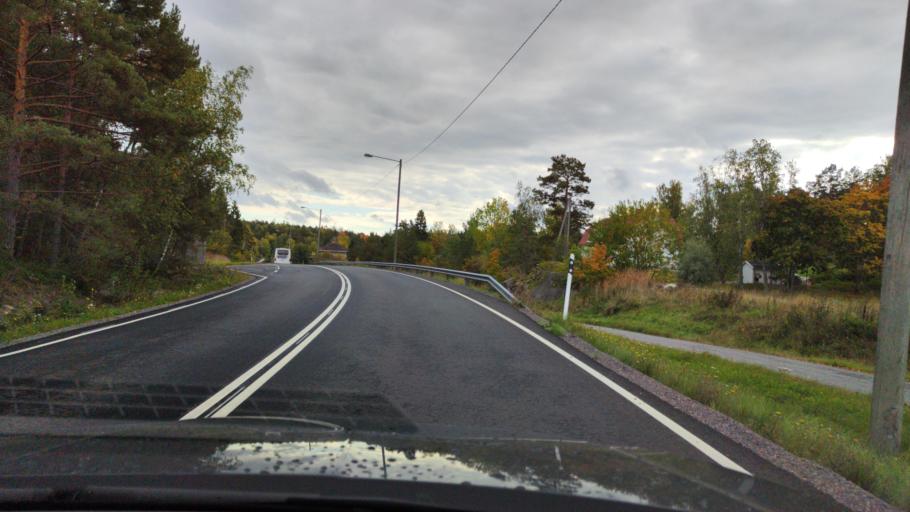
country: FI
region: Varsinais-Suomi
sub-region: Turku
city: Raisio
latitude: 60.3677
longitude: 22.1750
